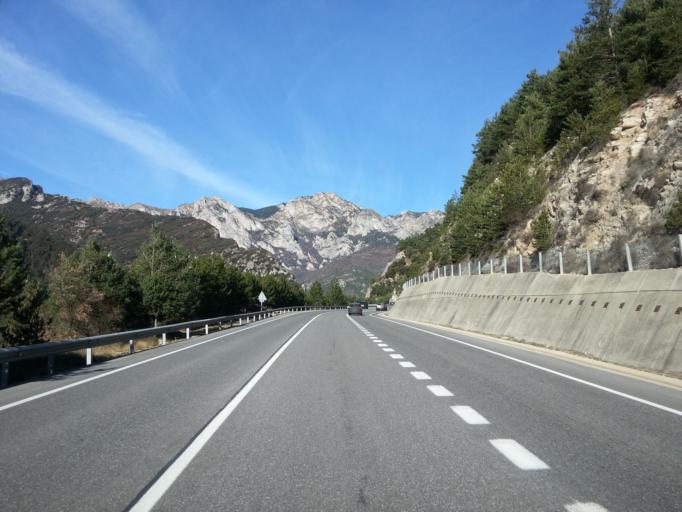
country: ES
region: Catalonia
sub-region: Provincia de Barcelona
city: Baga
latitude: 42.2628
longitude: 1.8526
